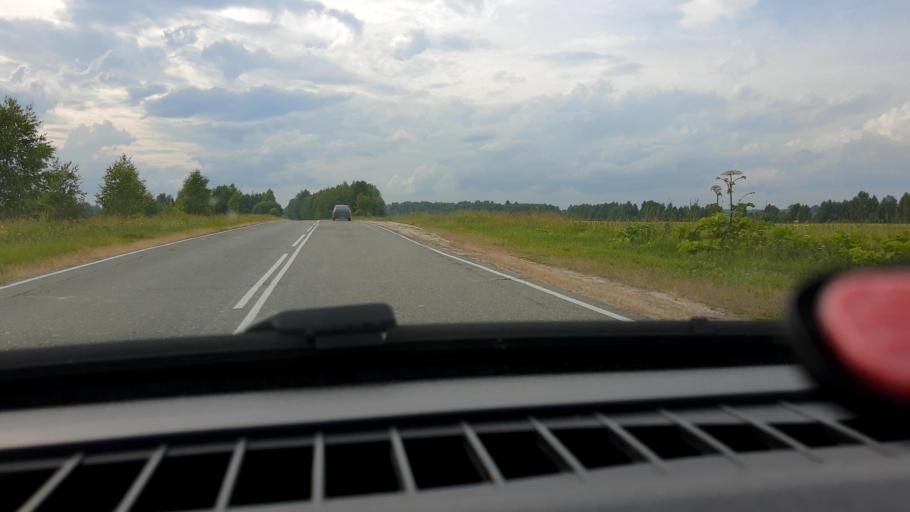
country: RU
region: Nizjnij Novgorod
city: Neklyudovo
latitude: 56.5062
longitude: 43.9730
